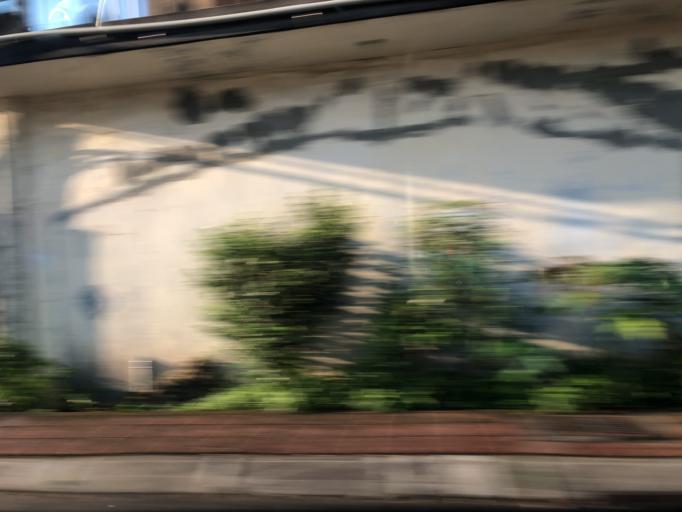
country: TW
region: Taiwan
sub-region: Yilan
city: Yilan
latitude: 24.7490
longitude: 121.7786
